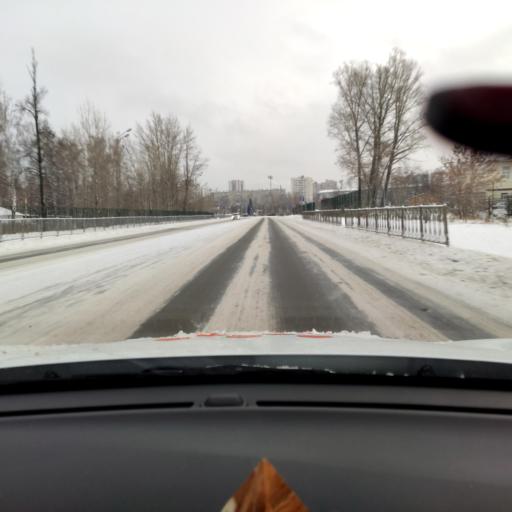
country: RU
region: Tatarstan
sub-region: Gorod Kazan'
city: Kazan
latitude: 55.7582
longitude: 49.1507
